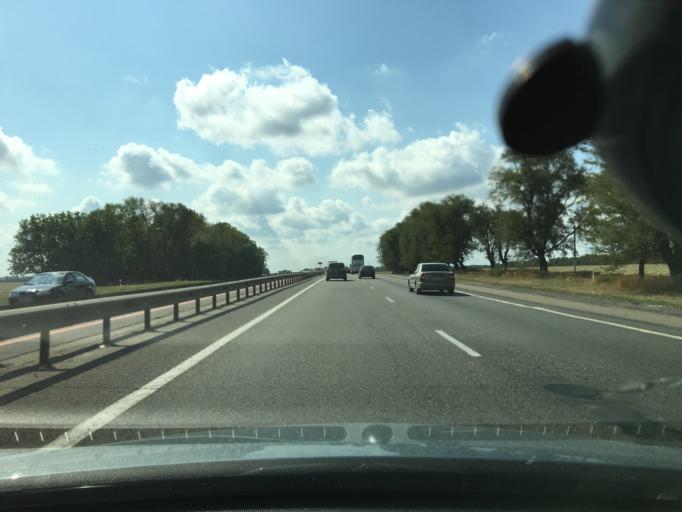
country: RU
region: Krasnodarskiy
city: Krasnoye
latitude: 46.7045
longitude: 39.6514
